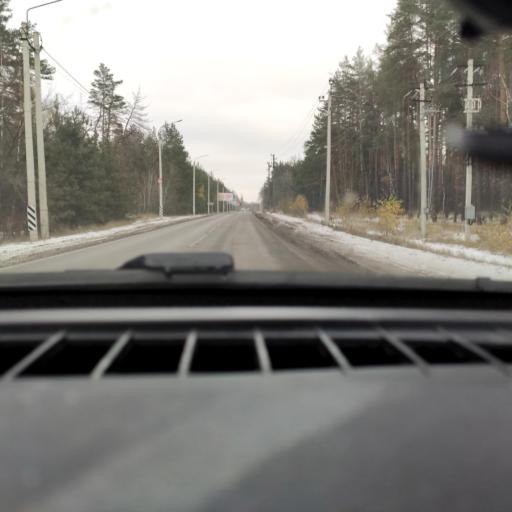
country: RU
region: Voronezj
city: Podgornoye
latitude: 51.7877
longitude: 39.1664
